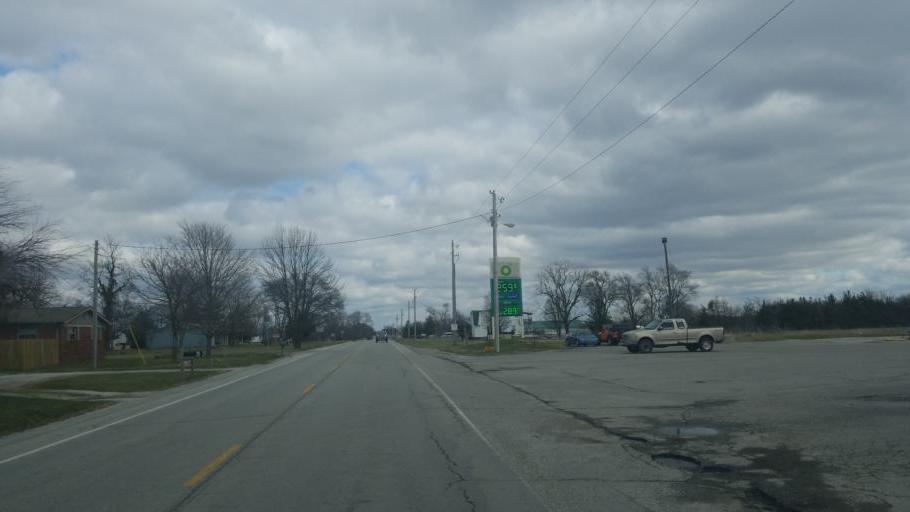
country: US
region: Indiana
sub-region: Putnam County
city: Greencastle
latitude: 39.7609
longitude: -86.7195
